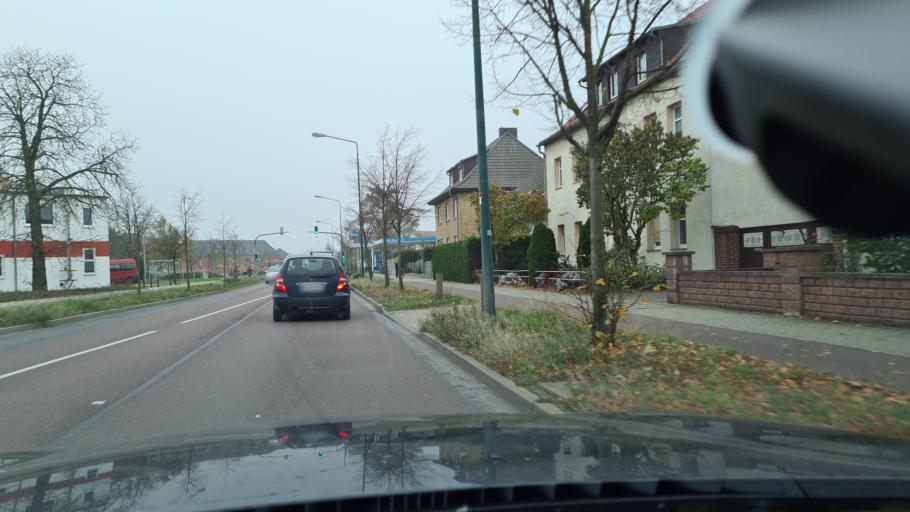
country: DE
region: Saxony-Anhalt
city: Wittenburg
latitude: 51.8804
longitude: 12.6535
